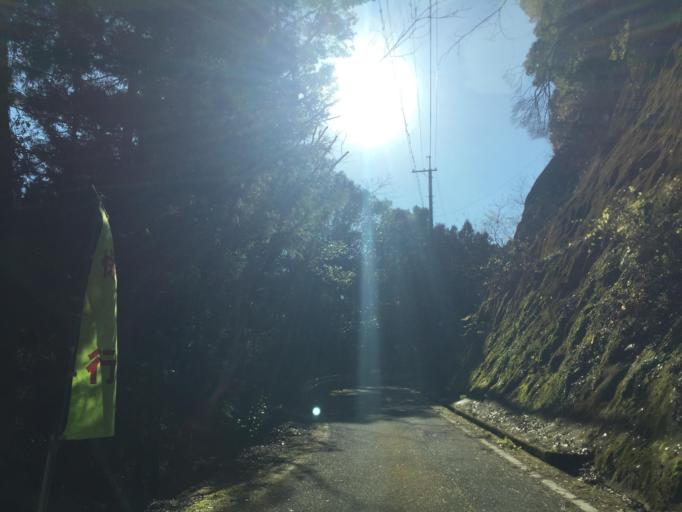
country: JP
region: Wakayama
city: Iwade
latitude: 34.1432
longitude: 135.4181
